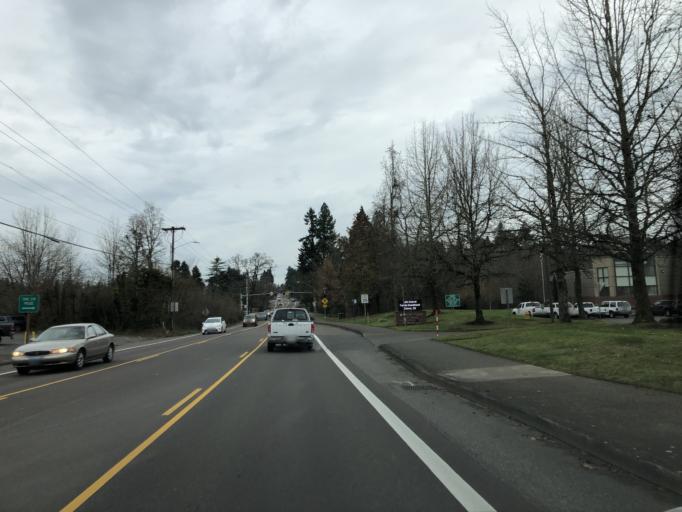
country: US
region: Oregon
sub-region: Washington County
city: Tigard
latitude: 45.4258
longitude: -122.7658
